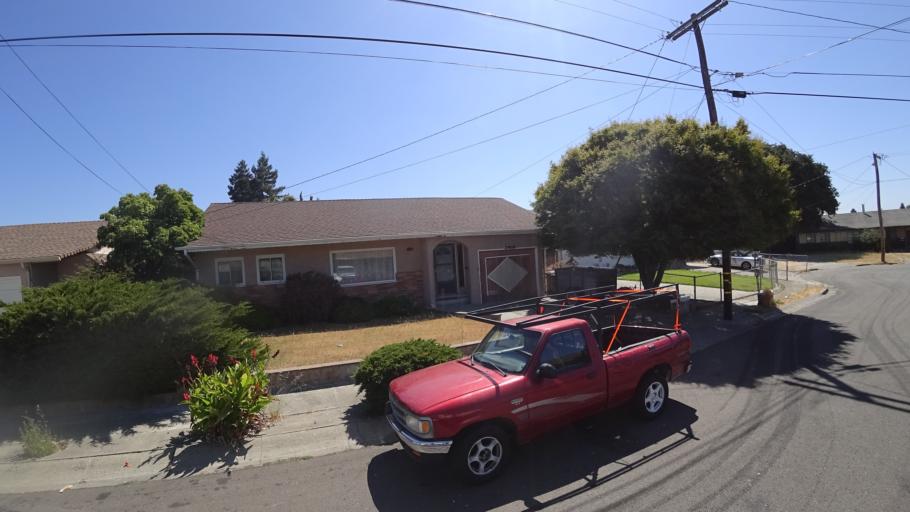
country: US
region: California
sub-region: Alameda County
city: Hayward
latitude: 37.6407
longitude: -122.0632
